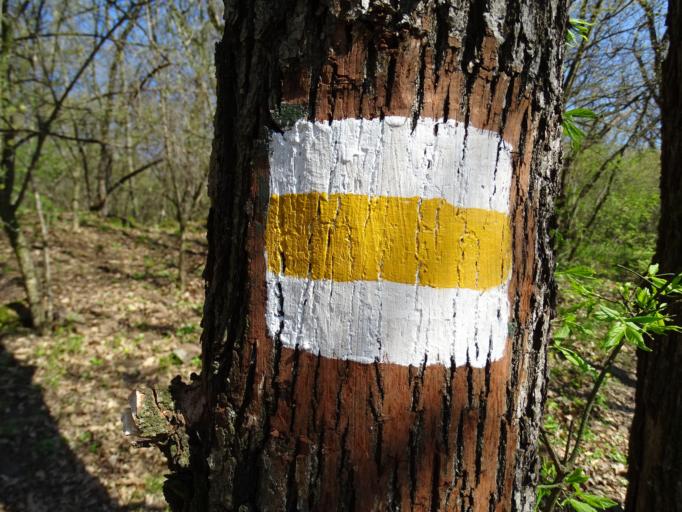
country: HU
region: Pest
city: Nagykovacsi
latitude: 47.6792
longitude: 19.0092
